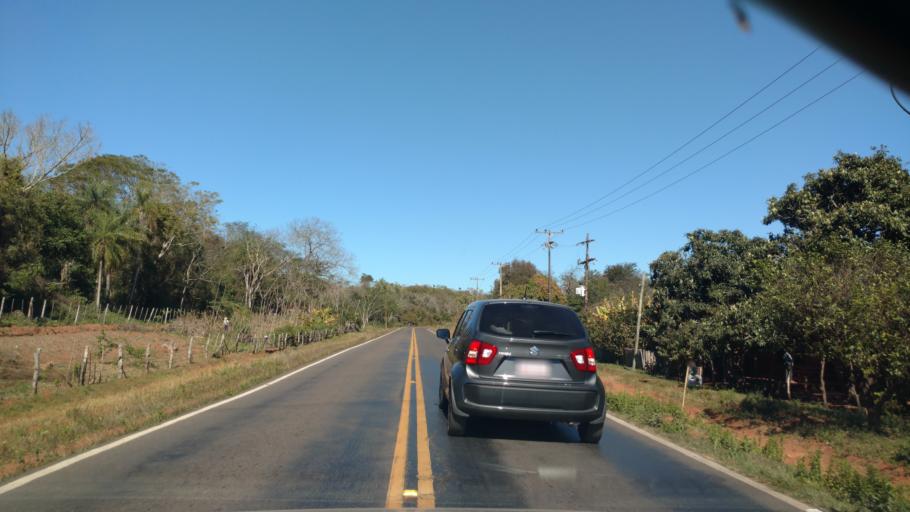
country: PY
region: Paraguari
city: Pirayu
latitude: -25.4969
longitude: -57.2465
